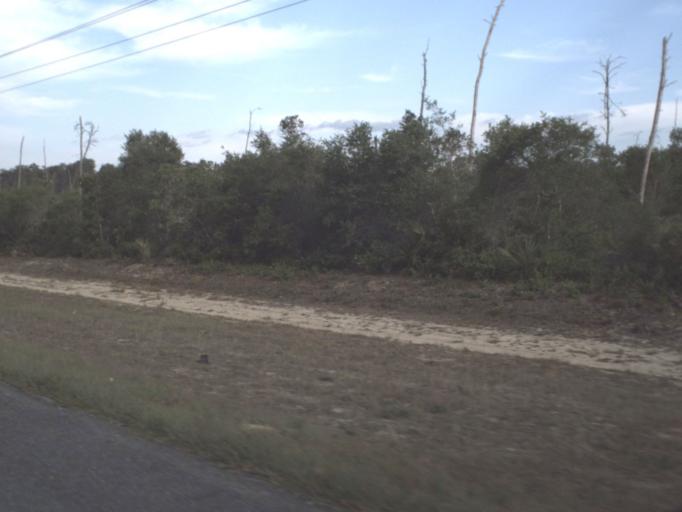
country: US
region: Florida
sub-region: Lake County
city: Astor
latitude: 29.1779
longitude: -81.7358
